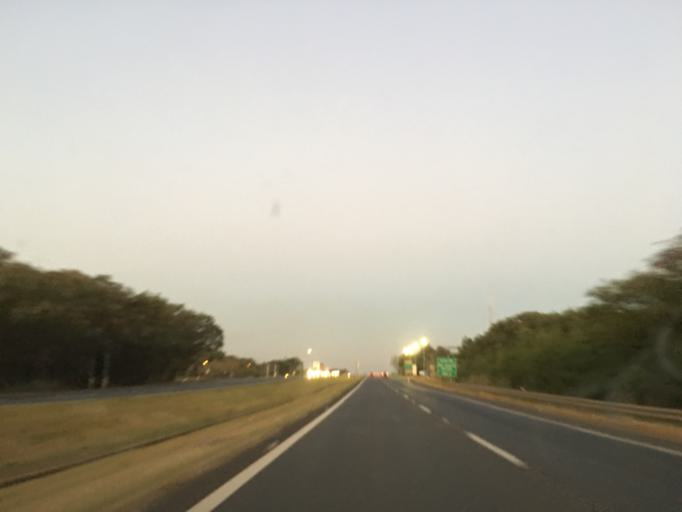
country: BR
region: Sao Paulo
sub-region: Piracicaba
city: Piracicaba
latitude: -22.7221
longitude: -47.6022
